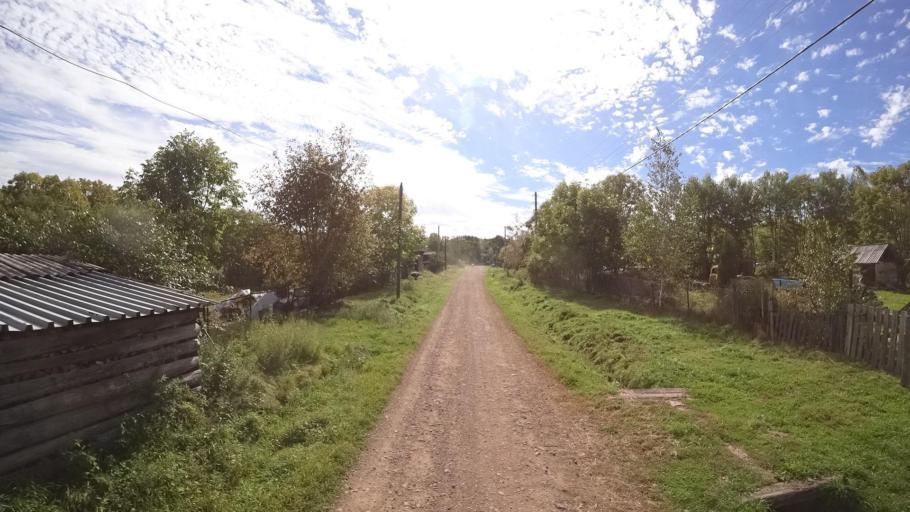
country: RU
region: Primorskiy
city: Yakovlevka
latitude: 44.3948
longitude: 133.5971
